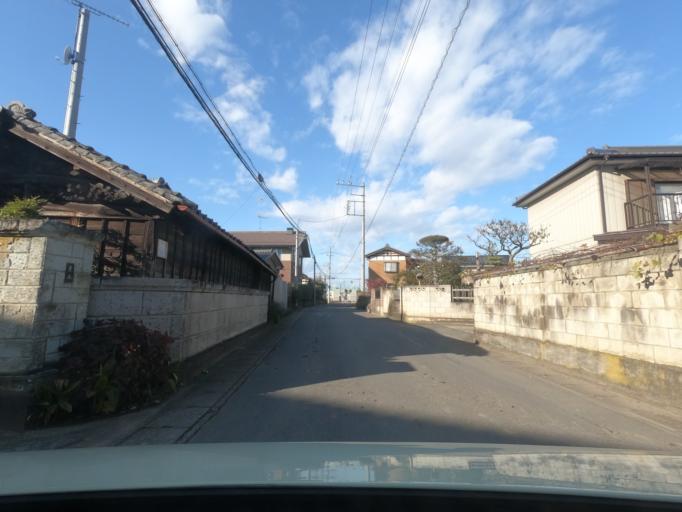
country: JP
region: Ibaraki
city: Koga
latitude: 36.2559
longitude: 139.7323
